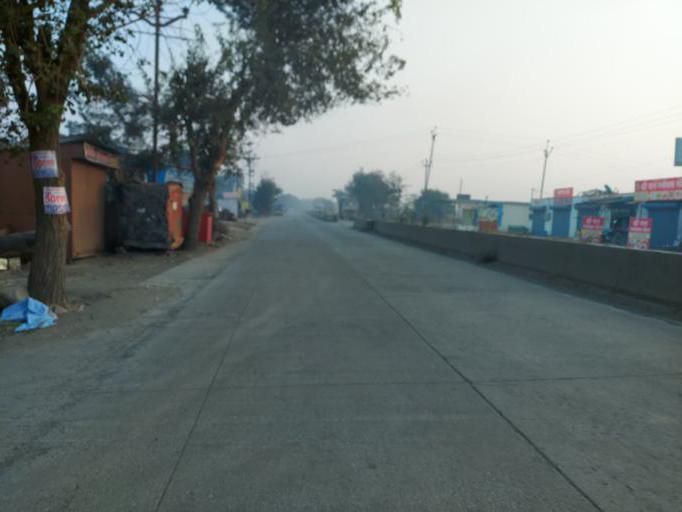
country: IN
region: Maharashtra
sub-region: Pune Division
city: Pune
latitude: 18.4635
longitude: 73.9520
